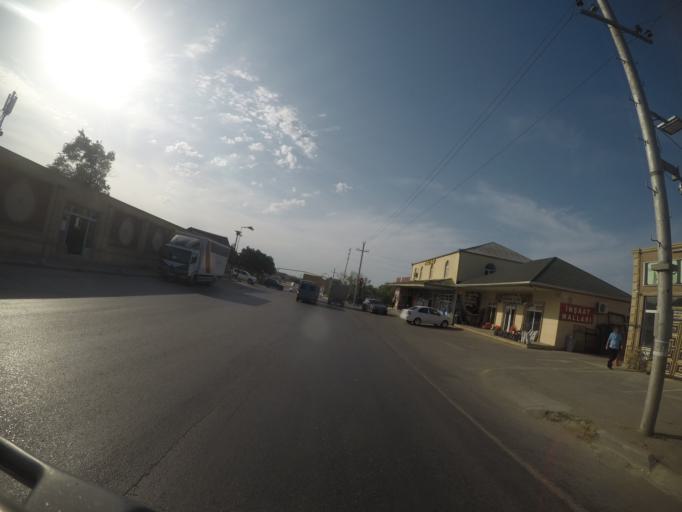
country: AZ
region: Baki
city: Binagadi
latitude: 40.4724
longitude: 49.8359
